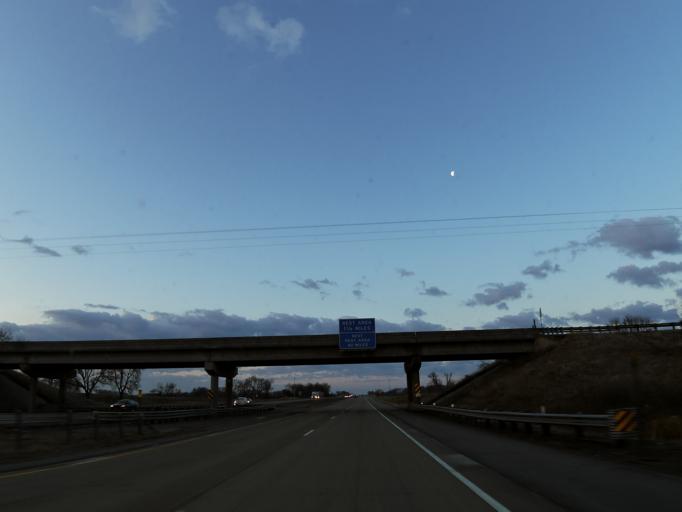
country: US
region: Minnesota
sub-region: Scott County
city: Elko New Market
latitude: 44.5738
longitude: -93.2986
